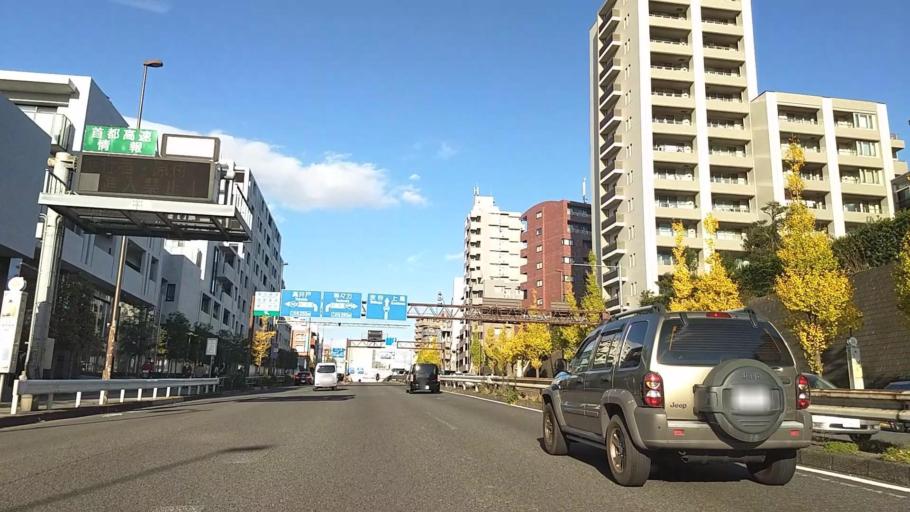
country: JP
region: Tokyo
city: Chofugaoka
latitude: 35.6188
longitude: 139.6290
